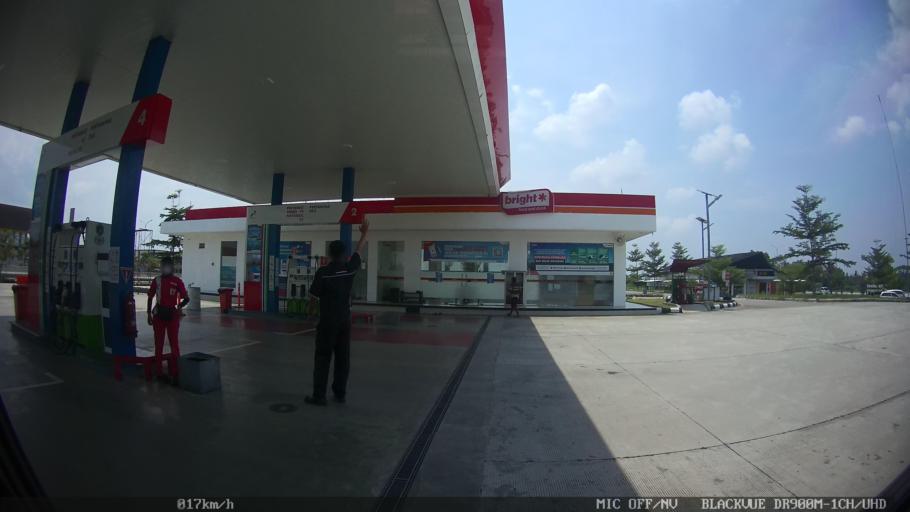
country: ID
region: Lampung
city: Kedaton
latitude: -5.3191
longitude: 105.2648
